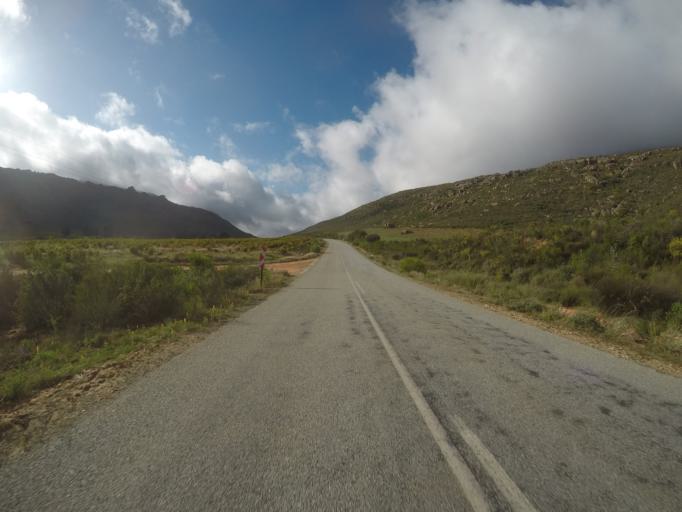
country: ZA
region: Western Cape
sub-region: West Coast District Municipality
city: Clanwilliam
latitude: -32.3629
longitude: 18.8563
